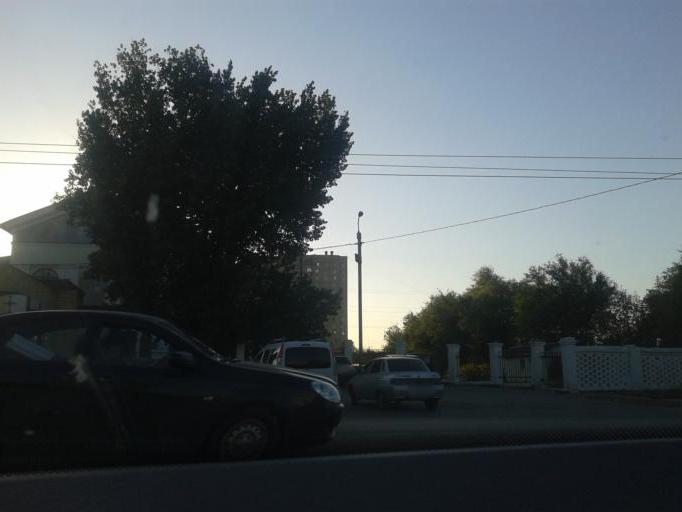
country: RU
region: Volgograd
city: Gorodishche
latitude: 48.7701
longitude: 44.4778
